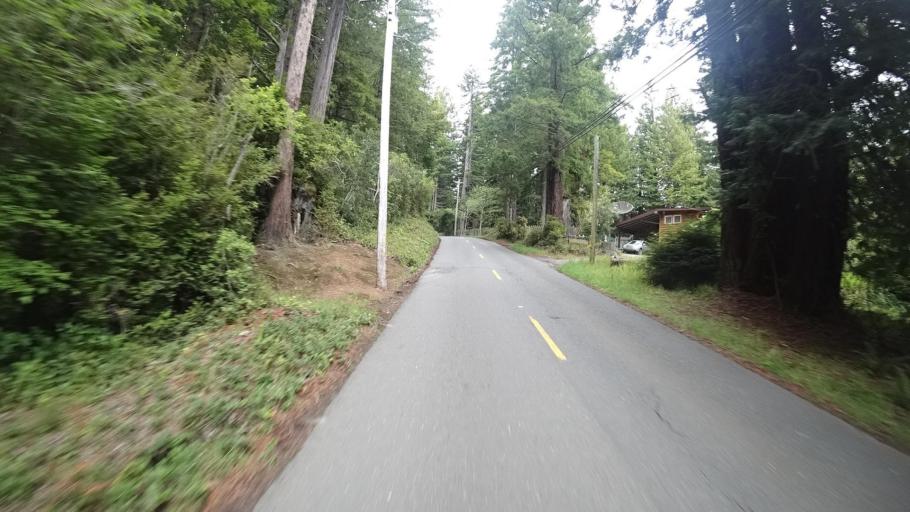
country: US
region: California
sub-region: Humboldt County
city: Bayside
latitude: 40.7911
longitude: -124.0557
